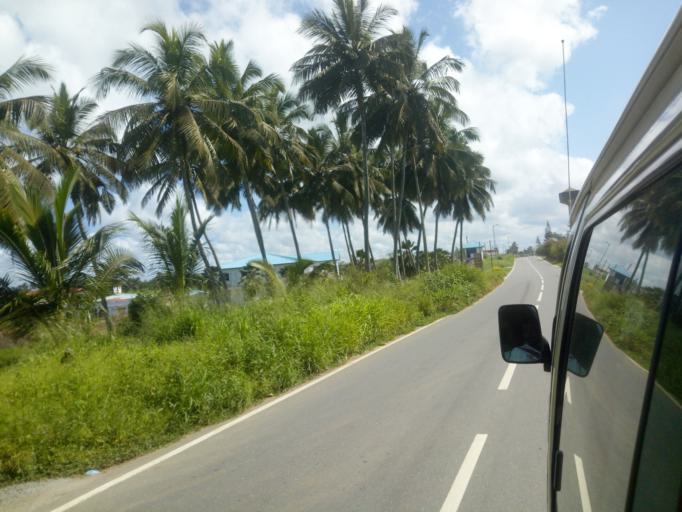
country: GH
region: Central
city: Elmina
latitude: 5.0933
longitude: -1.3391
